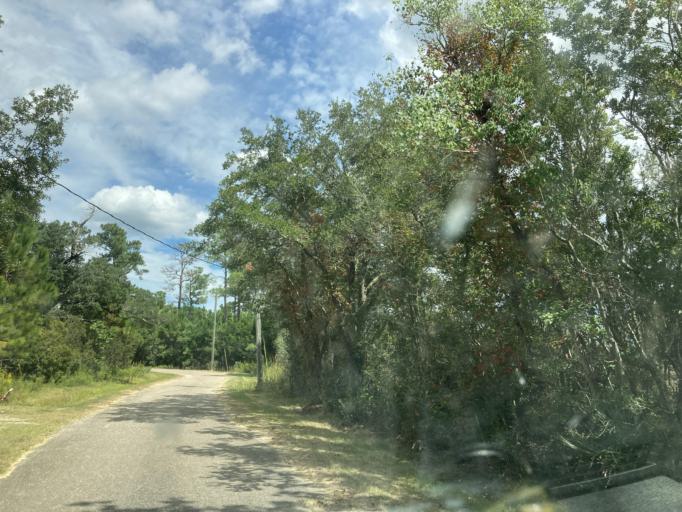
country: US
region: Mississippi
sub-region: Jackson County
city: Saint Martin
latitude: 30.4309
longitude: -88.8762
